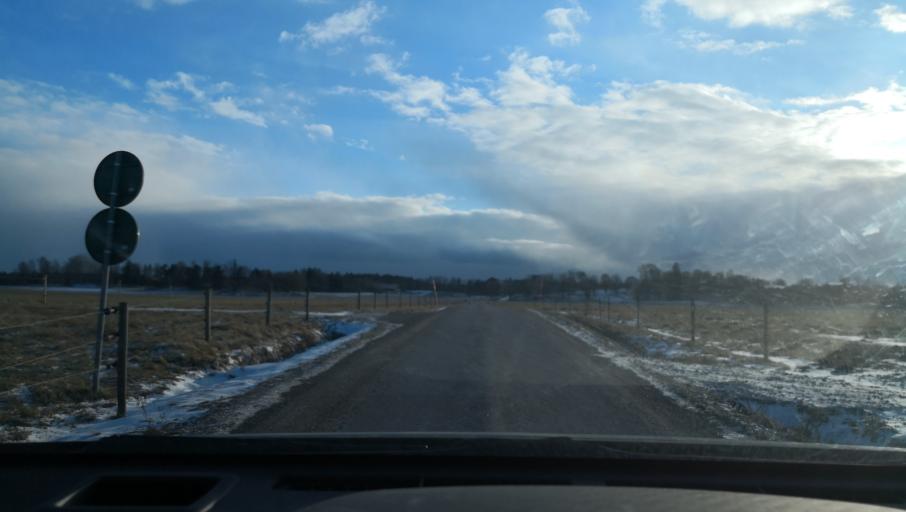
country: SE
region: Uppsala
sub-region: Enkopings Kommun
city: Irsta
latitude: 59.6587
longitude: 16.8059
